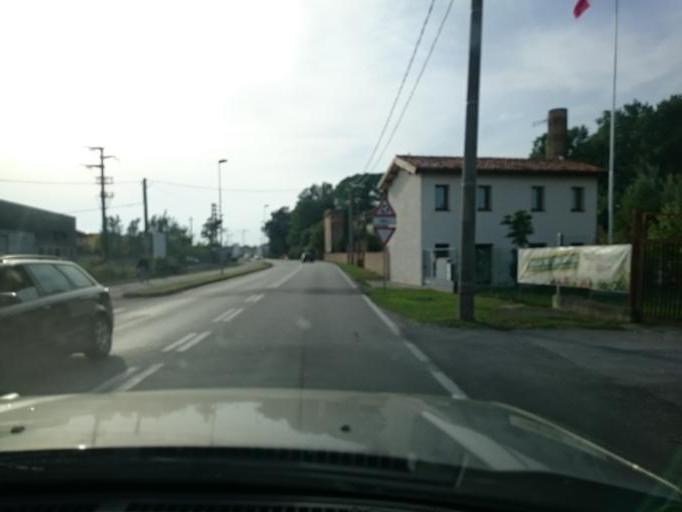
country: IT
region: Veneto
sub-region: Provincia di Padova
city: Oltre Brenta
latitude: 45.4094
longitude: 11.9910
